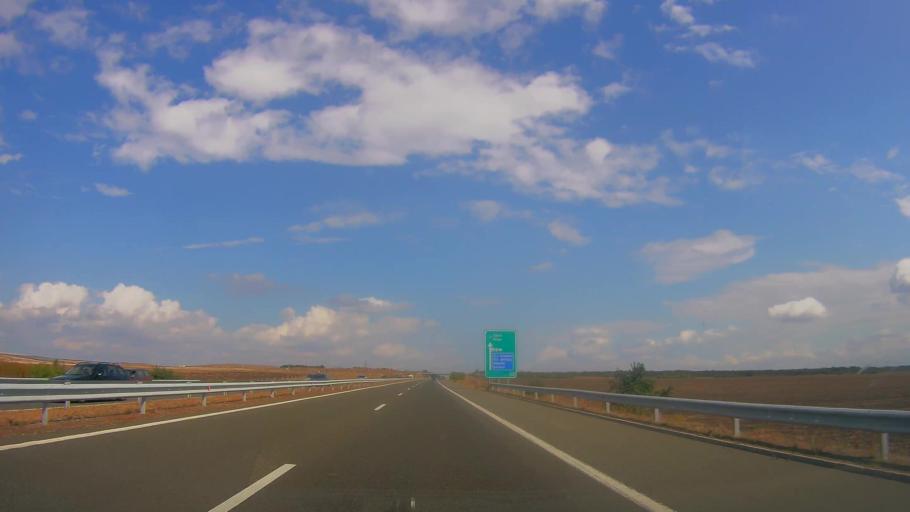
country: BG
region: Burgas
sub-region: Obshtina Karnobat
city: Karnobat
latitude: 42.5894
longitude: 26.9744
